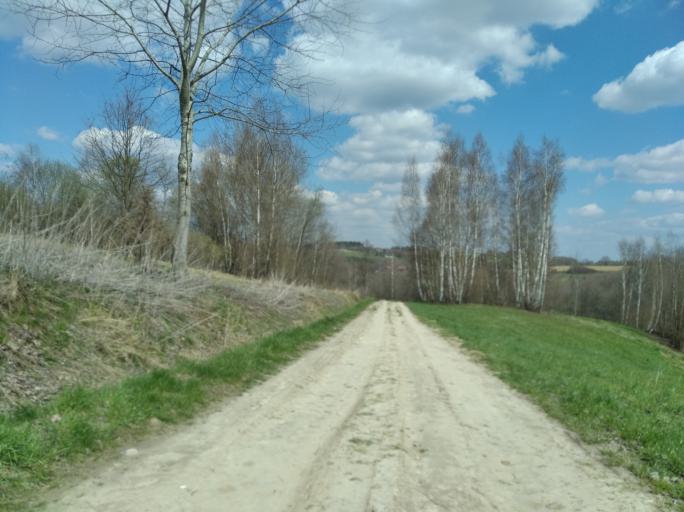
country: PL
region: Subcarpathian Voivodeship
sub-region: Powiat strzyzowski
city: Wysoka Strzyzowska
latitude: 49.8445
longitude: 21.7583
